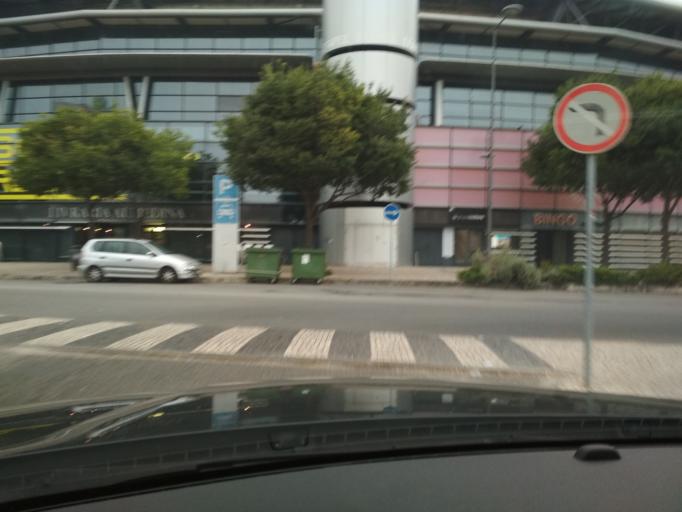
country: PT
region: Coimbra
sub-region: Coimbra
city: Coimbra
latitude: 40.2020
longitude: -8.4087
